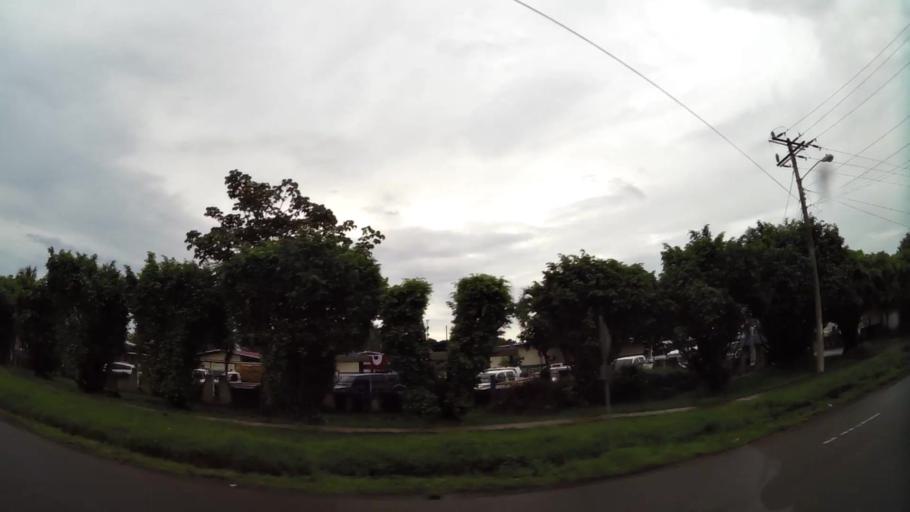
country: PA
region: Veraguas
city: Santiago de Veraguas
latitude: 8.1111
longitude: -80.9703
